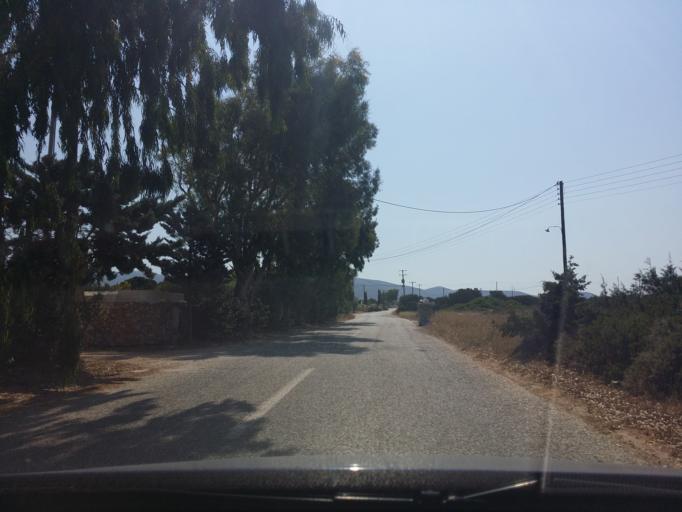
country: GR
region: South Aegean
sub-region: Nomos Kykladon
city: Antiparos
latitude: 37.0213
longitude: 25.1077
